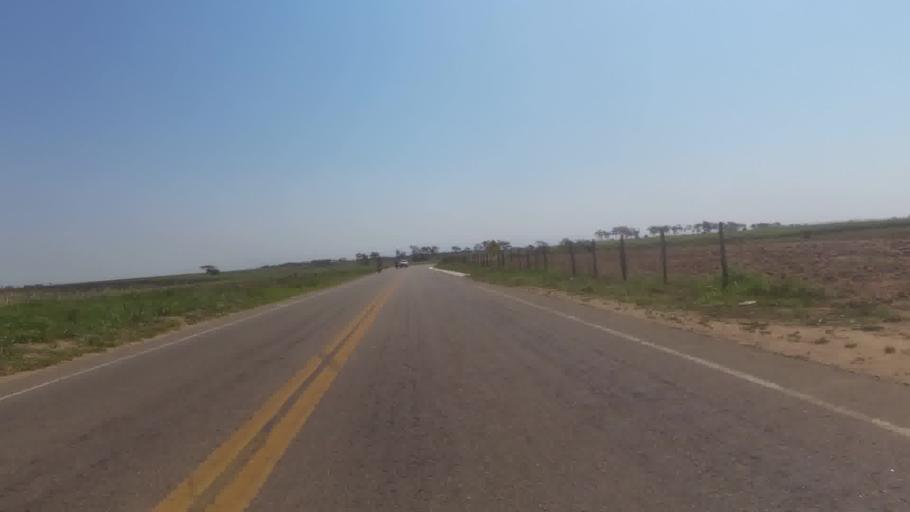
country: BR
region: Espirito Santo
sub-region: Marataizes
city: Marataizes
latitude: -21.0738
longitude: -40.8514
